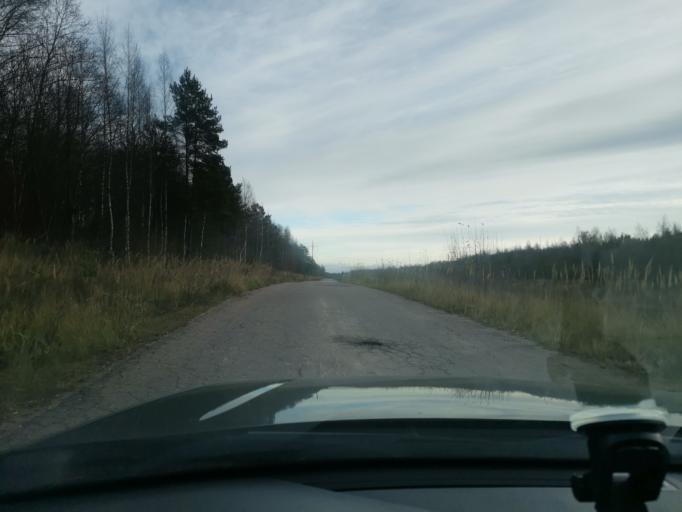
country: EE
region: Ida-Virumaa
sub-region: Sillamaee linn
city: Sillamae
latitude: 59.2655
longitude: 27.8988
